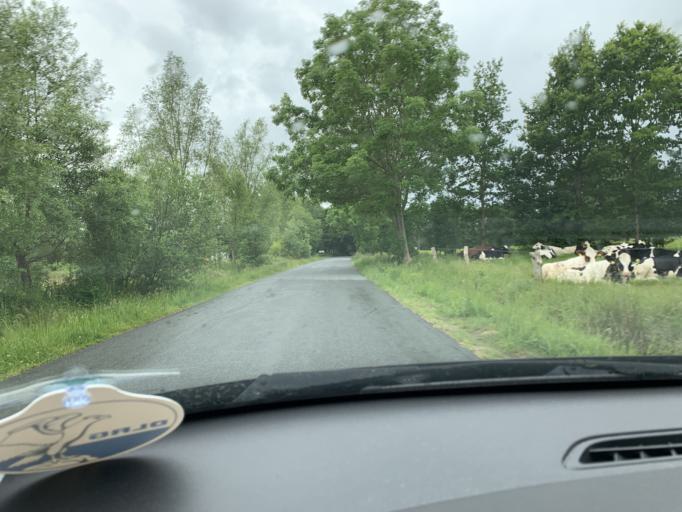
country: DE
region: Lower Saxony
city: Zetel
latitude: 53.4011
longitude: 7.9467
